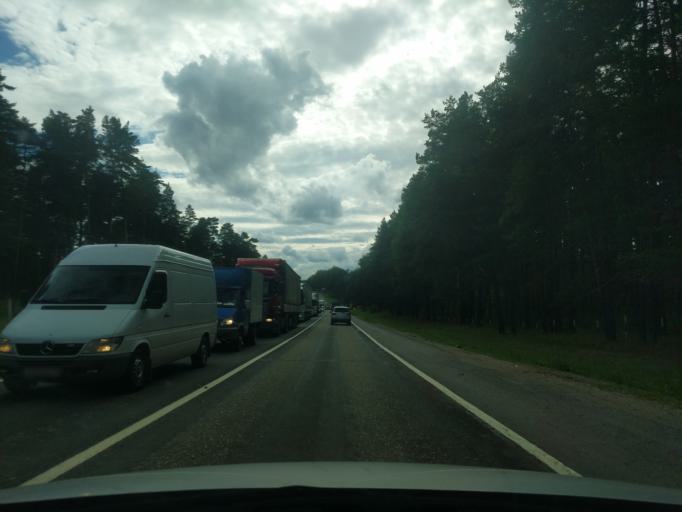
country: RU
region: Jaroslavl
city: Levashevo
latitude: 57.6742
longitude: 40.5857
